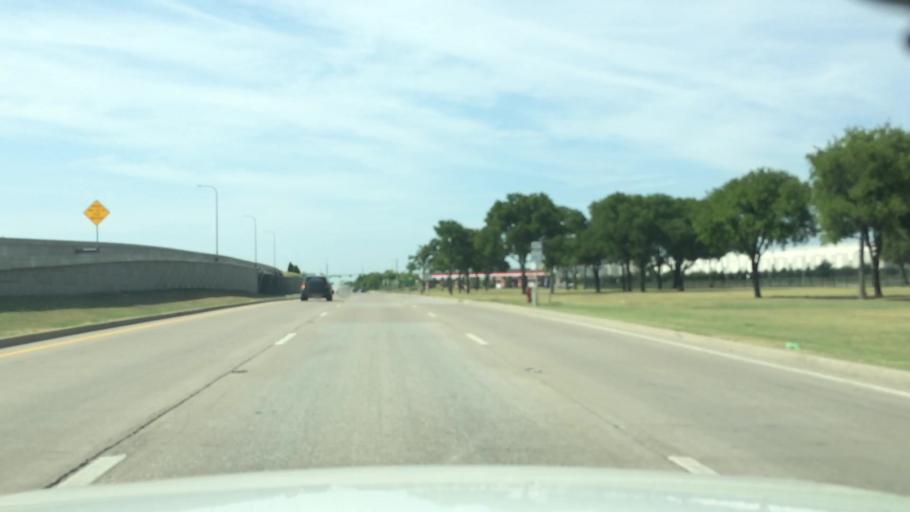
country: US
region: Texas
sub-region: Dallas County
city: Grand Prairie
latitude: 32.7123
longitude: -97.0251
